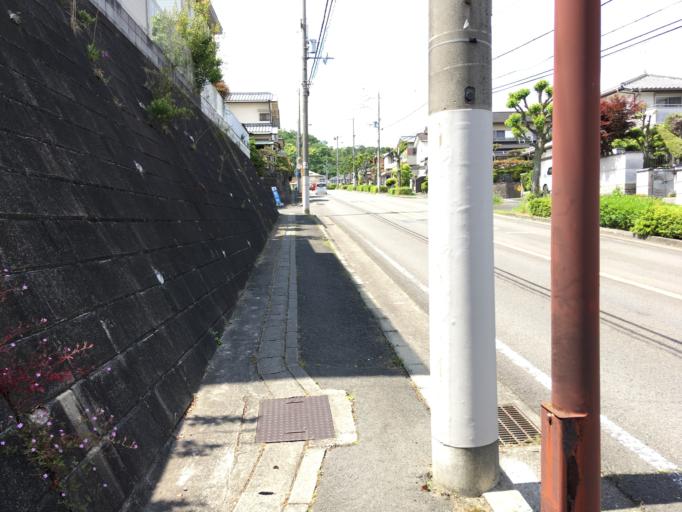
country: JP
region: Nara
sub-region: Ikoma-shi
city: Ikoma
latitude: 34.7130
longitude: 135.7149
